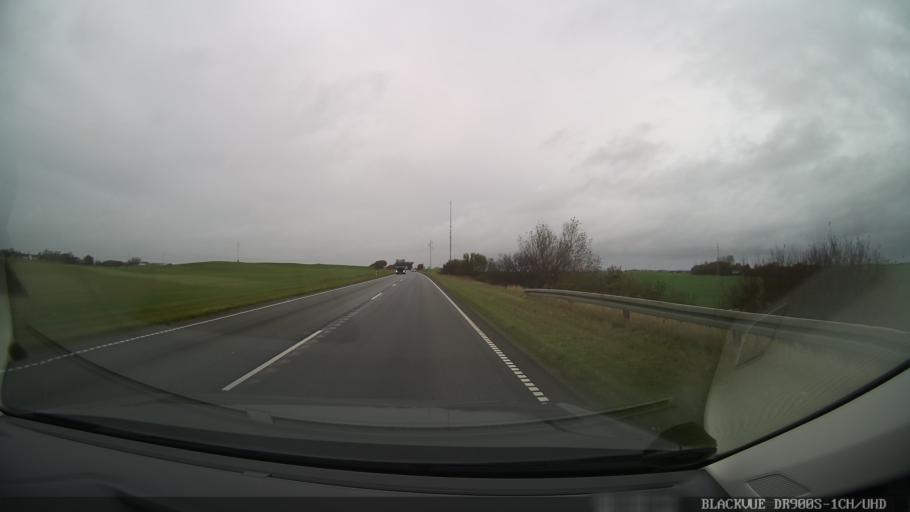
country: DK
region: North Denmark
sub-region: Morso Kommune
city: Nykobing Mors
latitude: 56.7945
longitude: 8.8126
